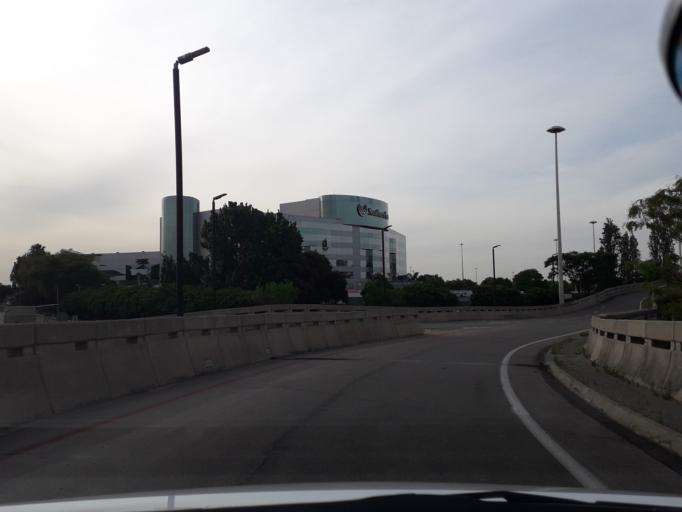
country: ZA
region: Gauteng
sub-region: City of Johannesburg Metropolitan Municipality
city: Modderfontein
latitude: -26.1358
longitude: 28.2288
